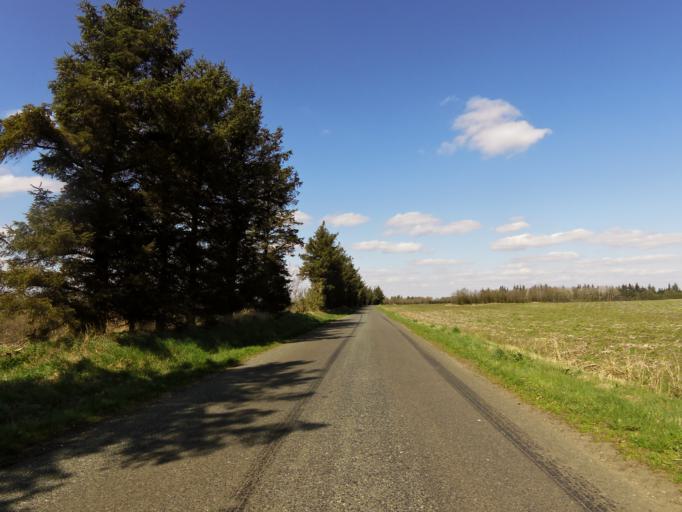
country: DK
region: South Denmark
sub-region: Esbjerg Kommune
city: Ribe
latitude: 55.3367
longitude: 8.8328
